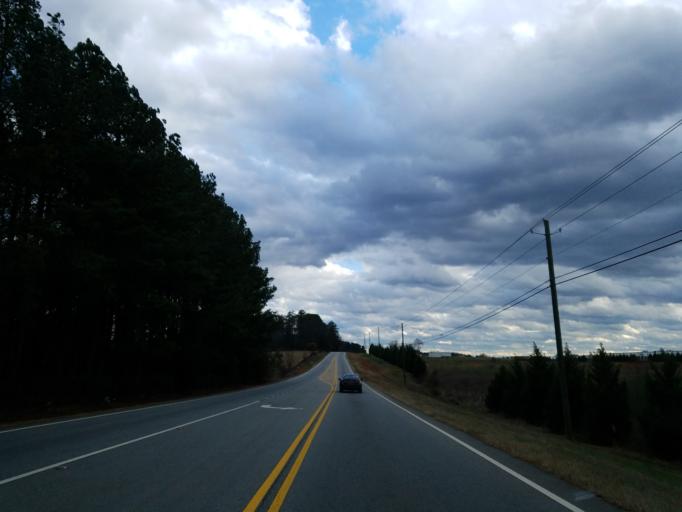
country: US
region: Georgia
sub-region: Henry County
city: McDonough
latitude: 33.4117
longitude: -84.1418
